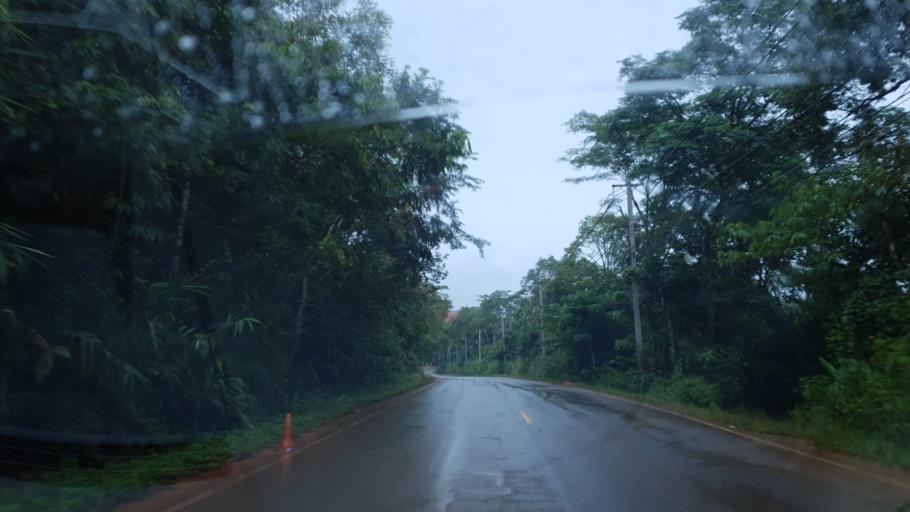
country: TH
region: Mae Hong Son
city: Ban Huai I Huak
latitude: 18.1410
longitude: 98.0748
